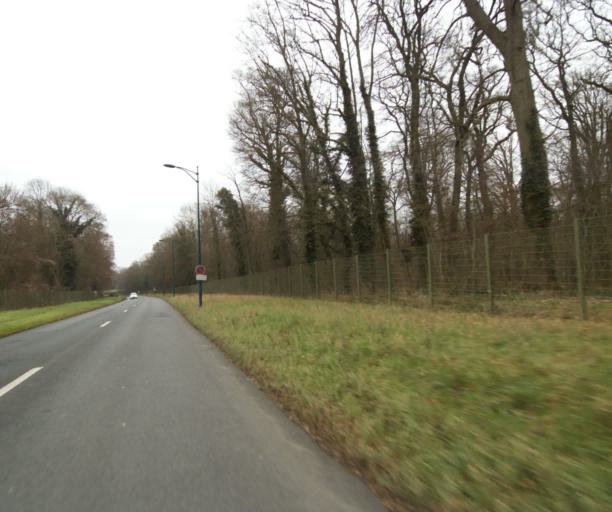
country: FR
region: Ile-de-France
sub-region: Departement des Hauts-de-Seine
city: Ville-d'Avray
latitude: 48.8336
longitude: 2.1994
